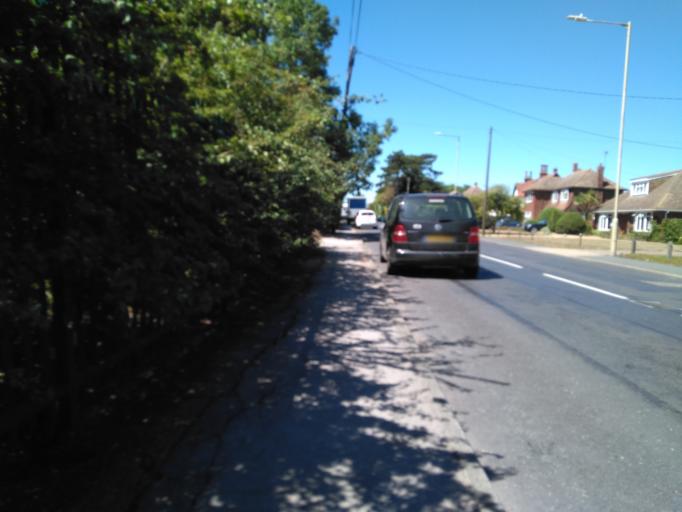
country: GB
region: England
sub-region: Kent
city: Tankerton
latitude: 51.3553
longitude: 1.0426
